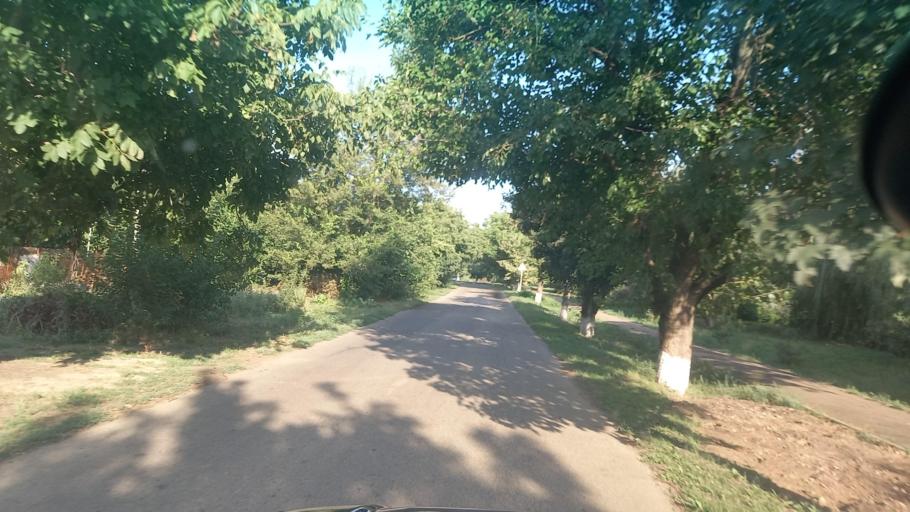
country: RU
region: Adygeya
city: Khatukay
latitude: 45.2925
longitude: 39.5583
